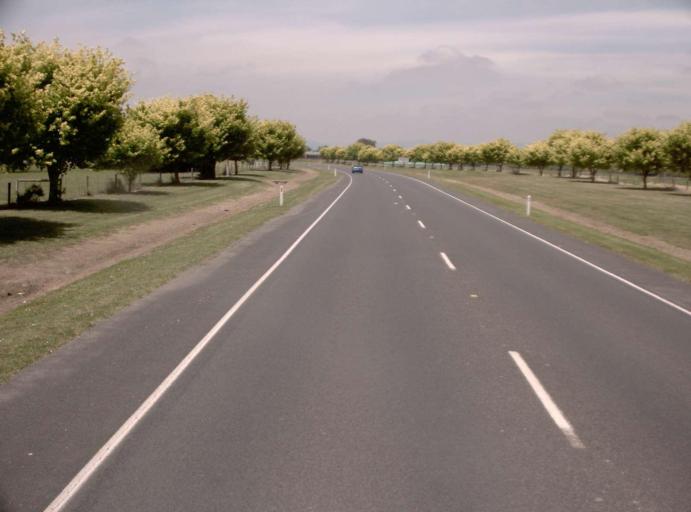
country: AU
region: Victoria
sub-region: Latrobe
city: Traralgon
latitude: -38.2044
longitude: 146.5443
